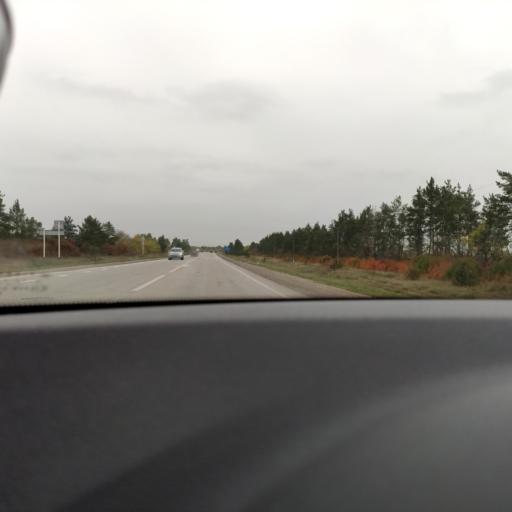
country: RU
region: Samara
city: Mirnyy
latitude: 53.5284
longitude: 50.3087
